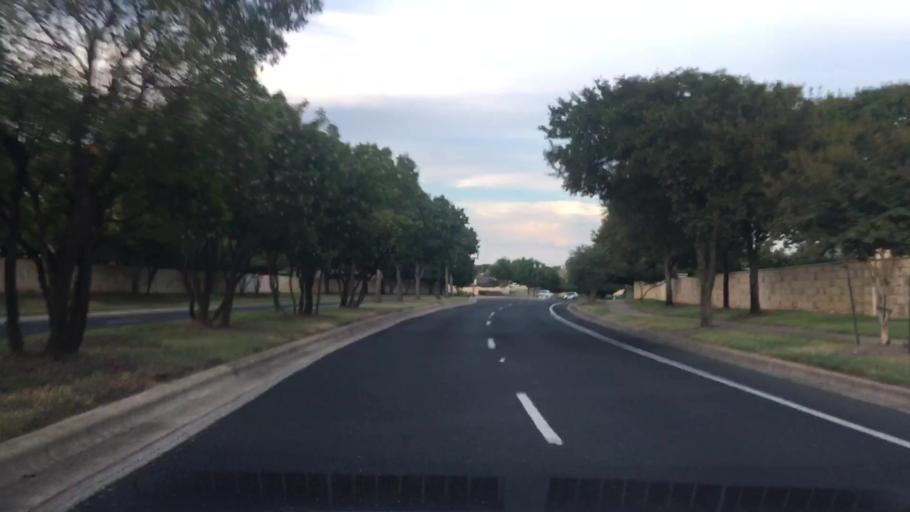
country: US
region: Texas
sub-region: Williamson County
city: Cedar Park
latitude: 30.4963
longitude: -97.7831
